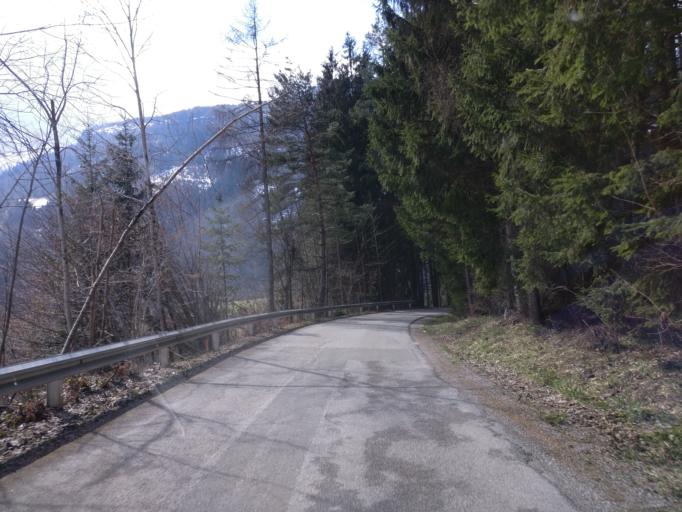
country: AT
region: Salzburg
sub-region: Politischer Bezirk Sankt Johann im Pongau
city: Bischofshofen
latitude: 47.4372
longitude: 13.2196
